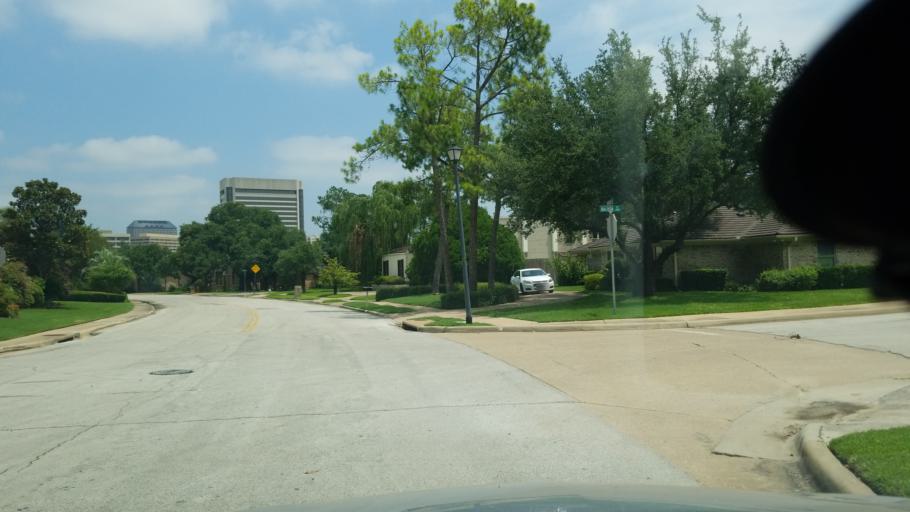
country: US
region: Texas
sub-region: Dallas County
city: Irving
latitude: 32.8572
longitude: -96.9417
